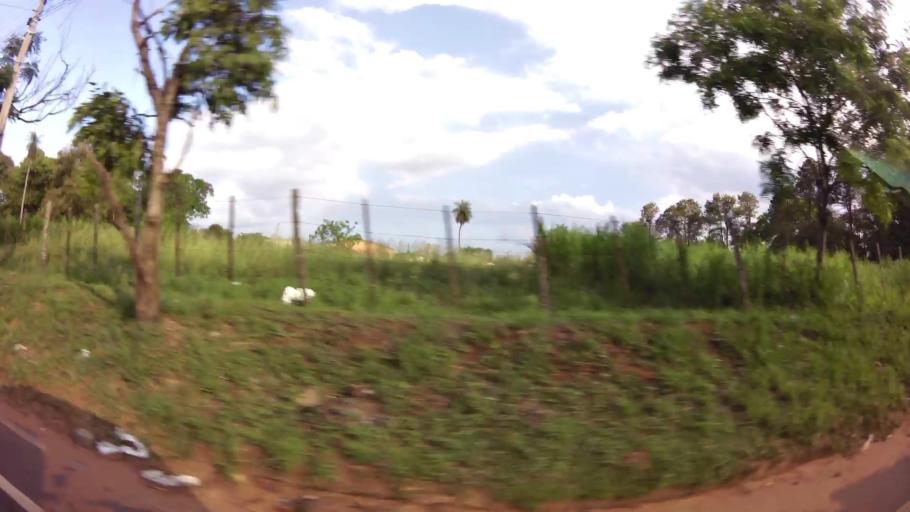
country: PY
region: Central
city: Fernando de la Mora
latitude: -25.3507
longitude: -57.5318
